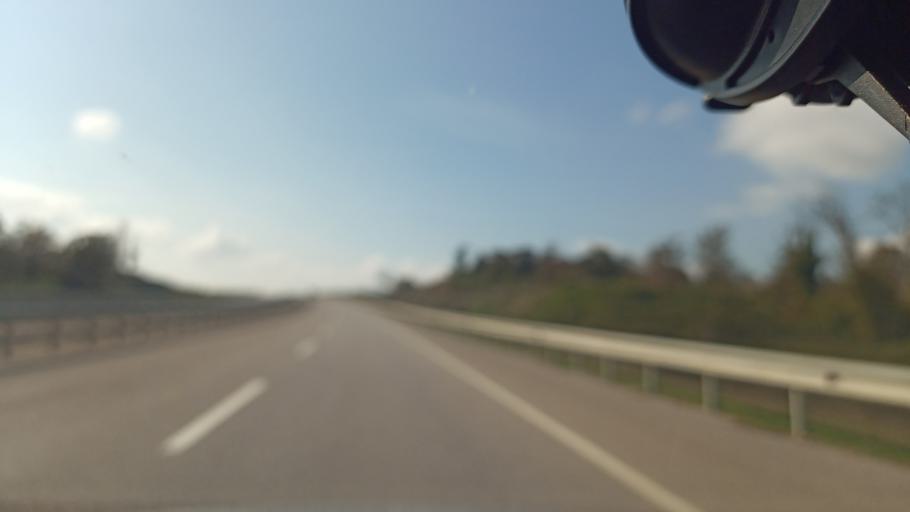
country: TR
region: Sakarya
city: Kaynarca
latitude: 41.0586
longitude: 30.3505
